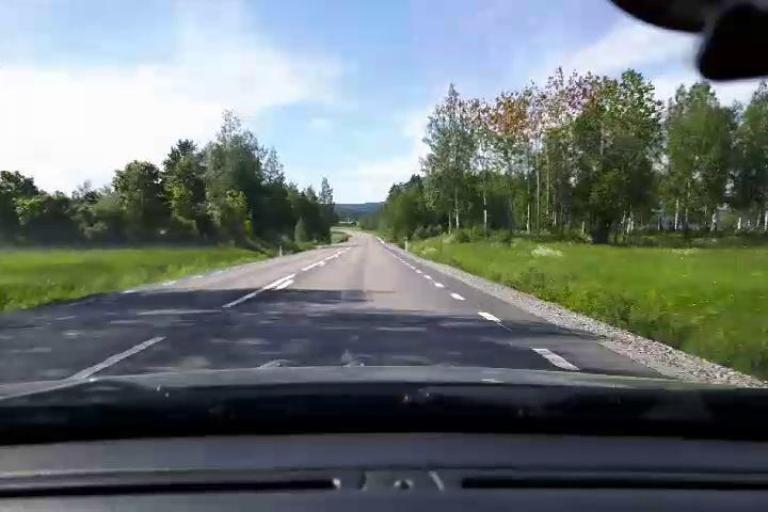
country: SE
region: Gaevleborg
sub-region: Bollnas Kommun
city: Kilafors
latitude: 61.1678
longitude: 16.8233
